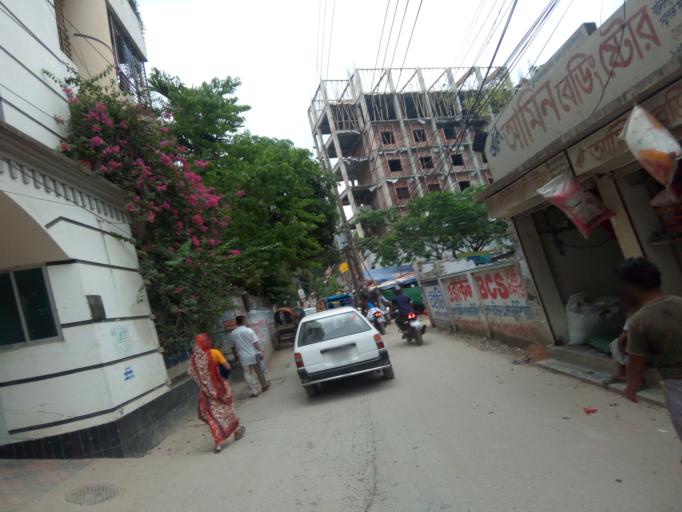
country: BD
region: Dhaka
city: Paltan
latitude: 23.7470
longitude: 90.4142
